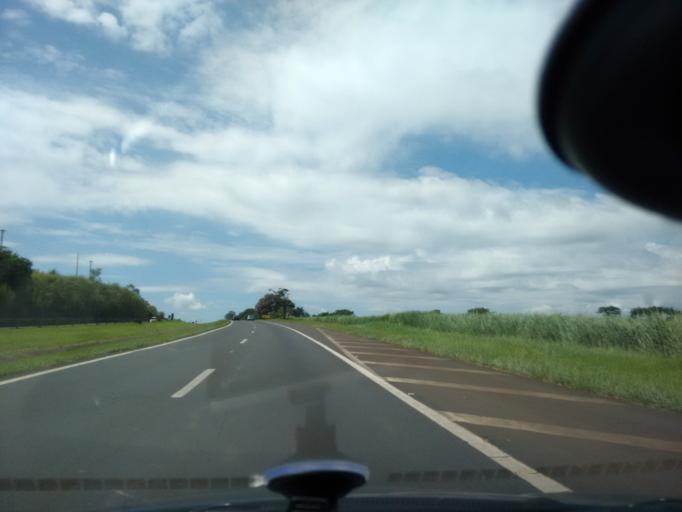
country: BR
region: Sao Paulo
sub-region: Ibate
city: Ibate
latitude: -21.8819
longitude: -48.0880
